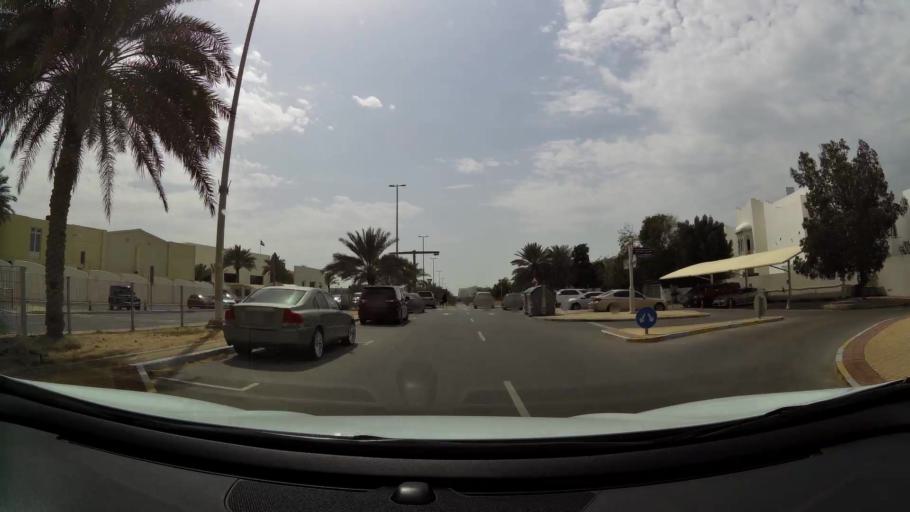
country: AE
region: Abu Dhabi
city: Abu Dhabi
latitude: 24.4649
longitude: 54.3406
